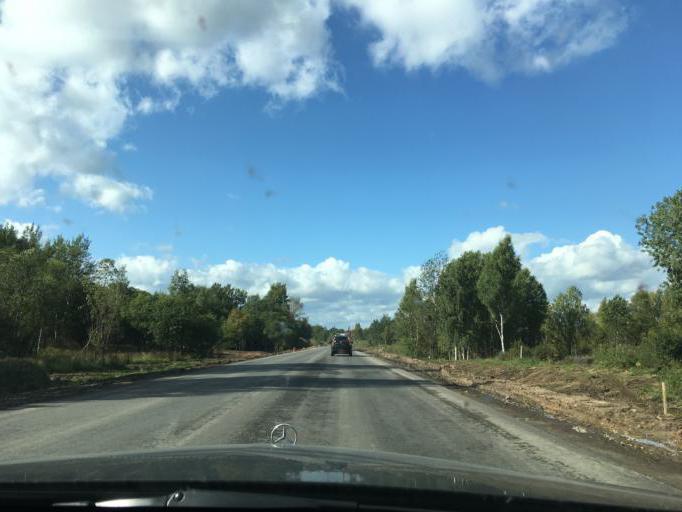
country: RU
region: Pskov
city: Velikiye Luki
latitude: 56.2711
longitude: 30.3648
